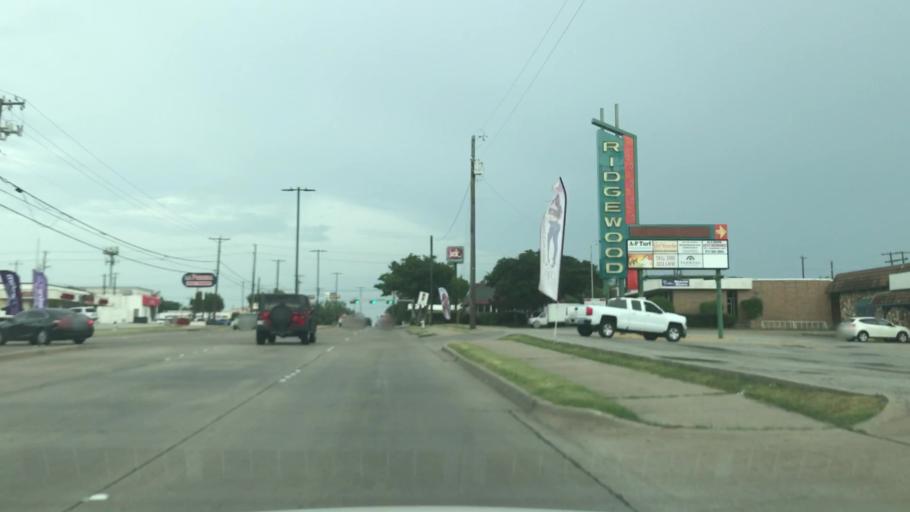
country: US
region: Texas
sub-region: Dallas County
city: Garland
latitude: 32.8788
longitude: -96.6328
